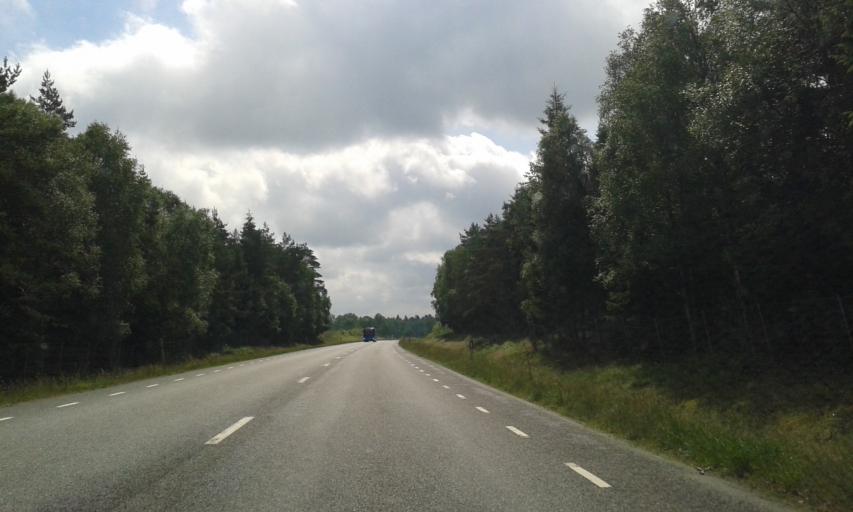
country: SE
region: Vaestra Goetaland
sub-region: Tranemo Kommun
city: Limmared
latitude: 57.5491
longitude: 13.3223
